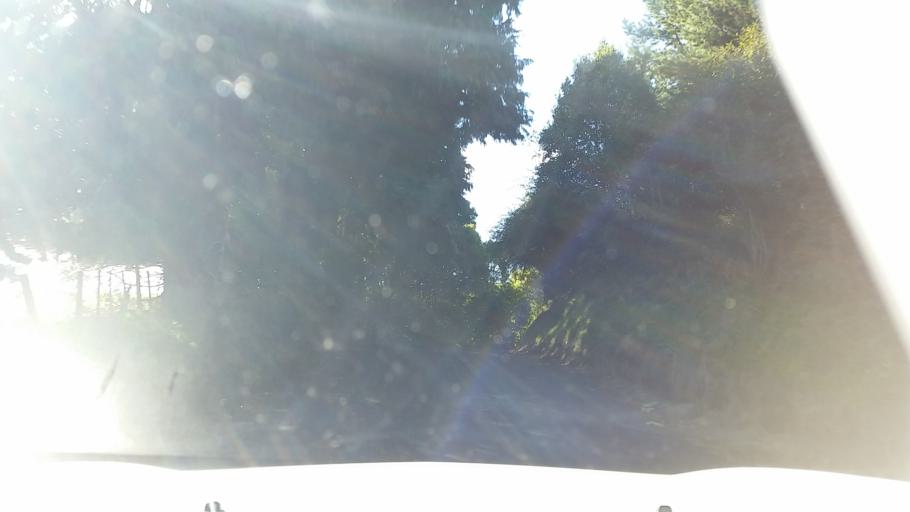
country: NZ
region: Waikato
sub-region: Matamata-Piako District
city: Matamata
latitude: -37.8229
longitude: 175.6389
